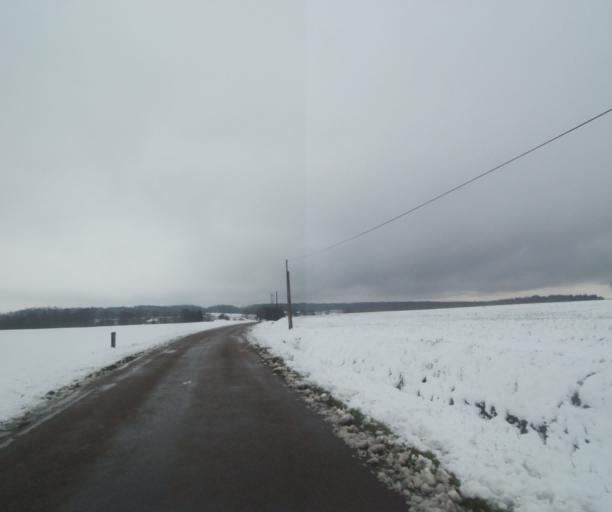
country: FR
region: Champagne-Ardenne
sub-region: Departement de la Haute-Marne
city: Laneuville-a-Remy
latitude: 48.5066
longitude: 4.8513
